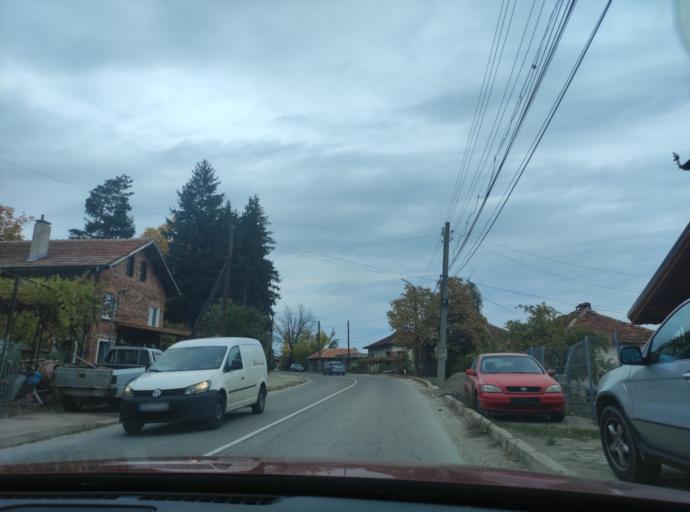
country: BG
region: Montana
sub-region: Obshtina Berkovitsa
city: Berkovitsa
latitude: 43.2034
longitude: 23.1613
